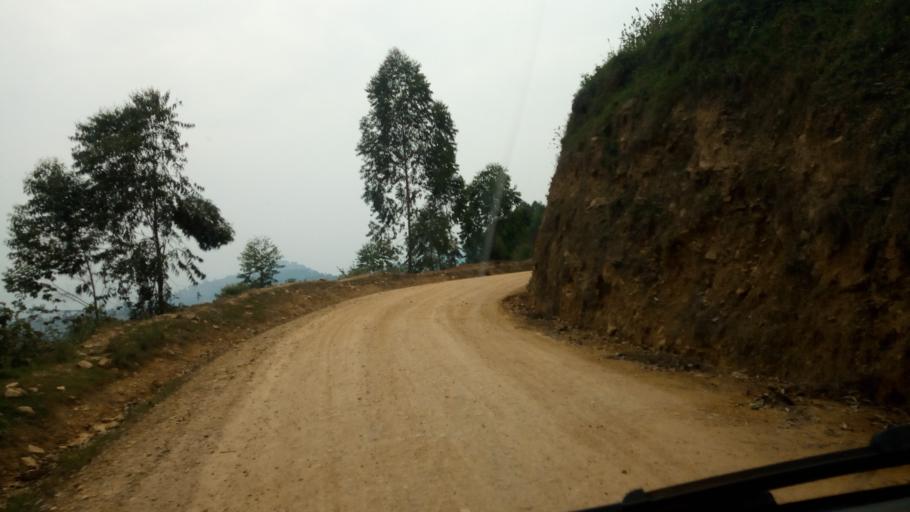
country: UG
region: Western Region
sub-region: Kanungu District
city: Kanungu
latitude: -1.0978
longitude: 29.8508
